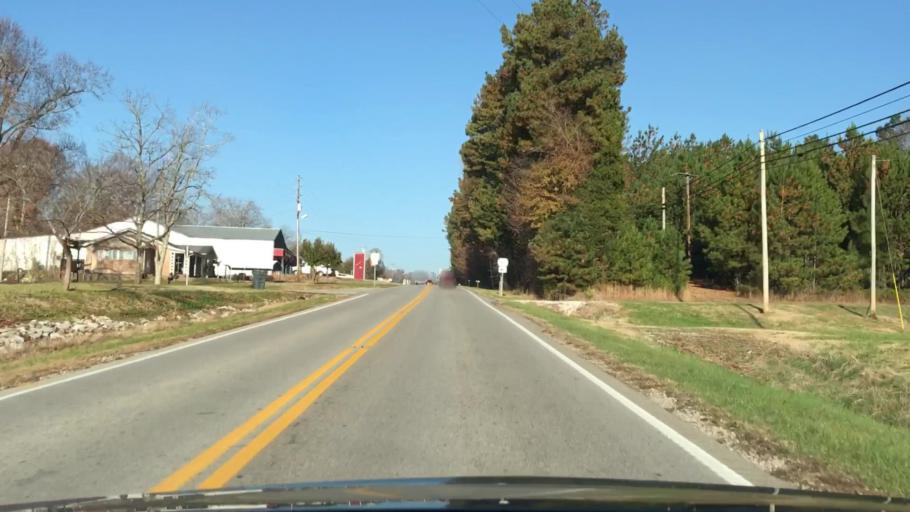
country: US
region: Kentucky
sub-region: Edmonson County
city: Brownsville
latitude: 37.2001
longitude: -86.2762
